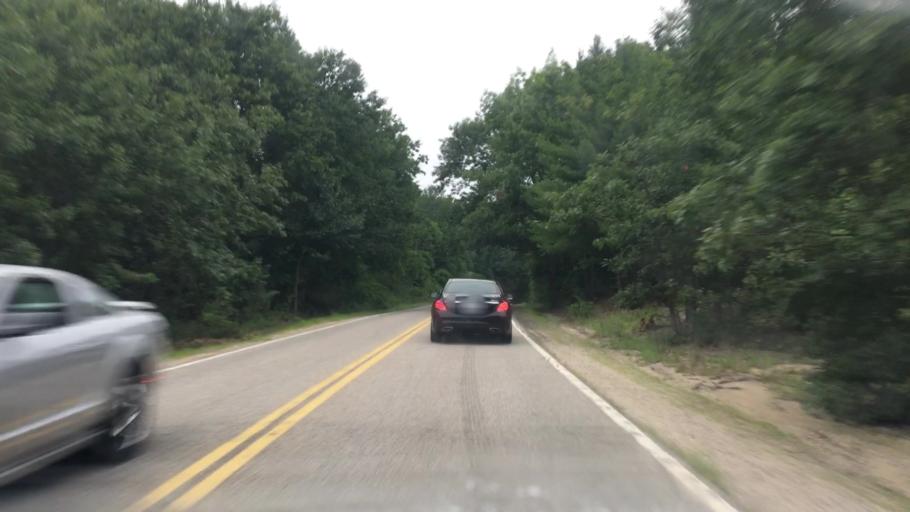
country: US
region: New Hampshire
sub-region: Rockingham County
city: Greenland
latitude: 43.0860
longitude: -70.8358
